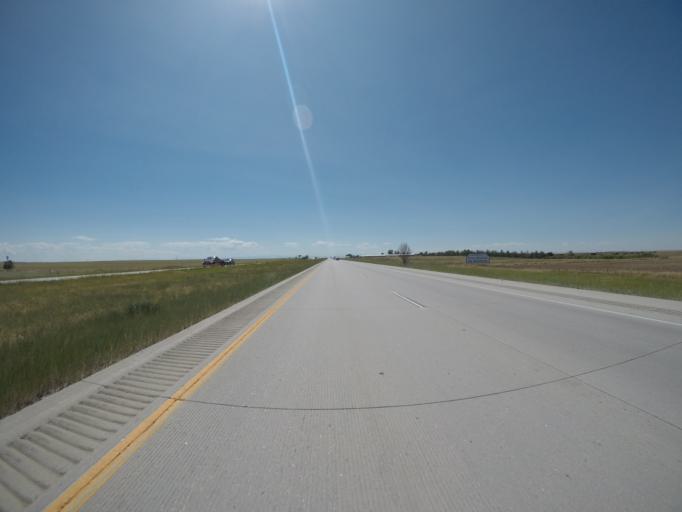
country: US
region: Colorado
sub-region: Adams County
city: Bennett
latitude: 39.7387
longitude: -104.5166
